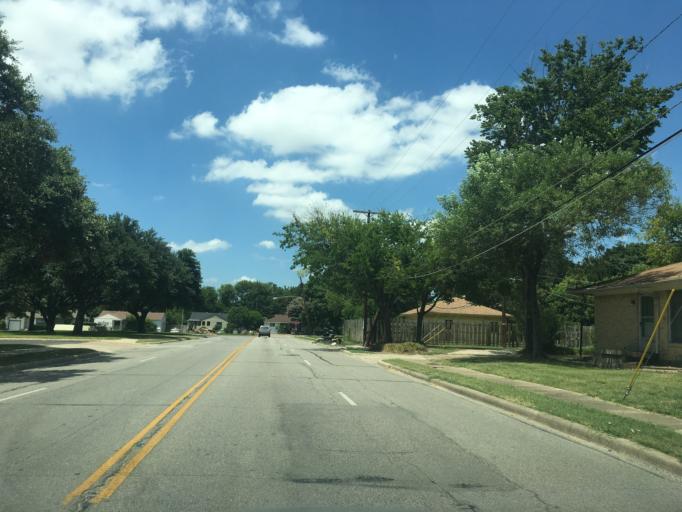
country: US
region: Texas
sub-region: Dallas County
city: Garland
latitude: 32.8337
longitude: -96.6681
